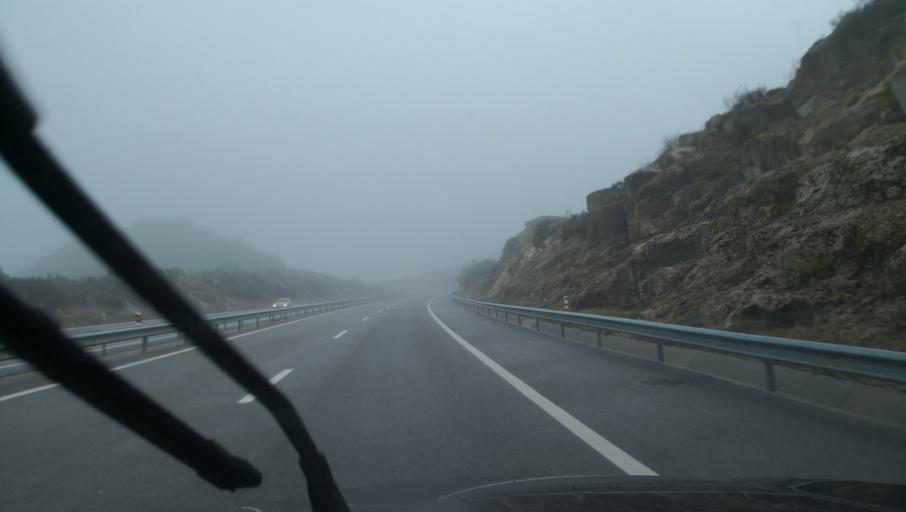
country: PT
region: Vila Real
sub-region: Vila Pouca de Aguiar
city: Vila Pouca de Aguiar
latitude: 41.4036
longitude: -7.6441
